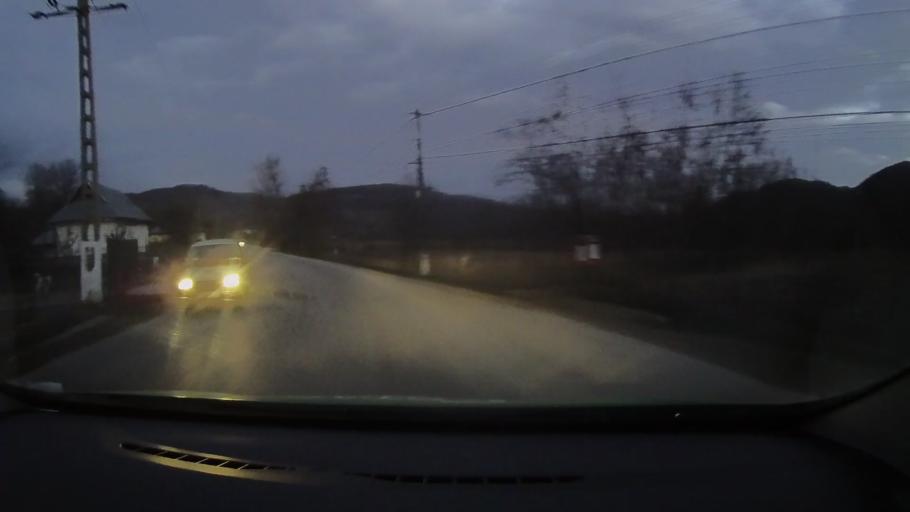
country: RO
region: Prahova
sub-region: Comuna Provita de Jos
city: Provita de Jos
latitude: 45.1205
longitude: 25.6619
